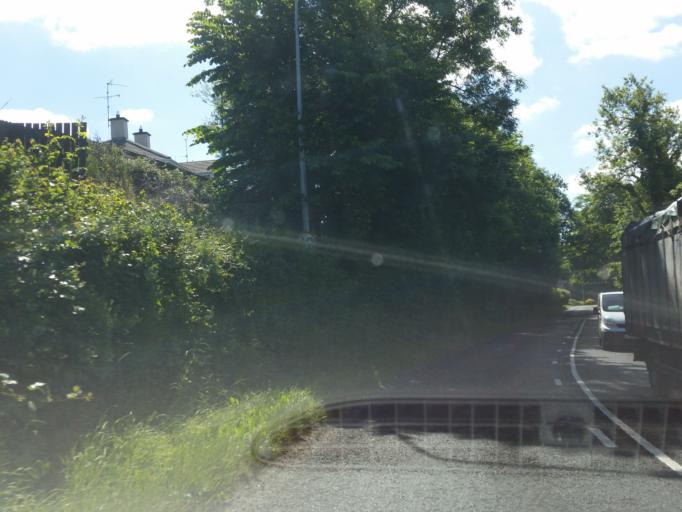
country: GB
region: Northern Ireland
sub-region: Fermanagh District
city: Enniskillen
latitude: 54.3563
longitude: -7.6269
